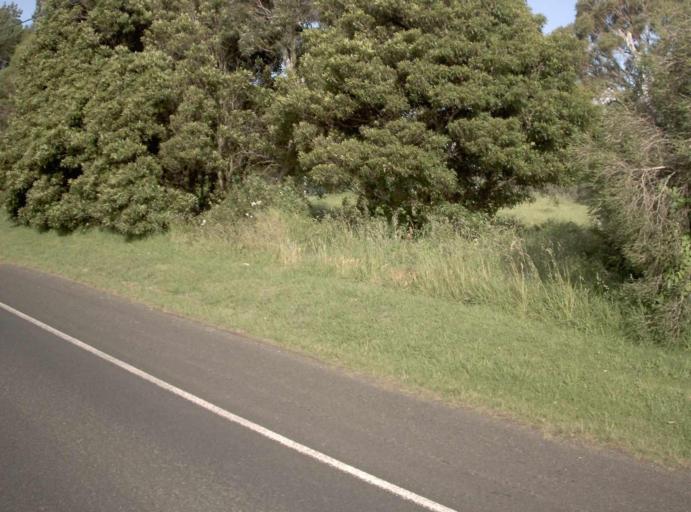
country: AU
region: Victoria
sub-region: Baw Baw
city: Warragul
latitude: -38.4872
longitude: 145.9352
